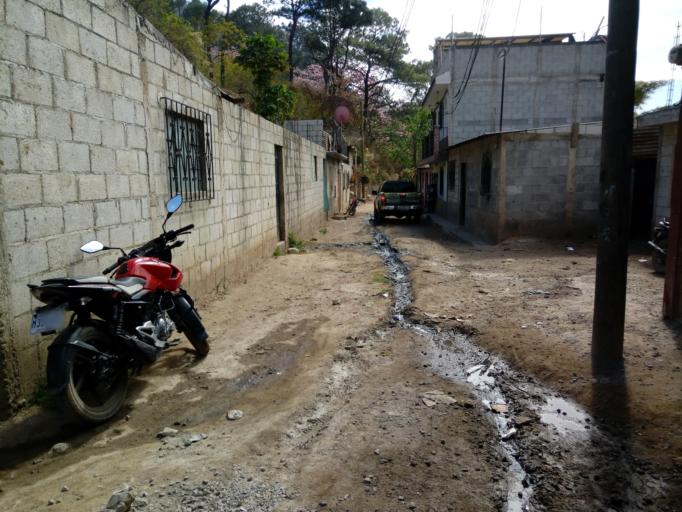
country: GT
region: Guatemala
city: Amatitlan
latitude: 14.4946
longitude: -90.6251
